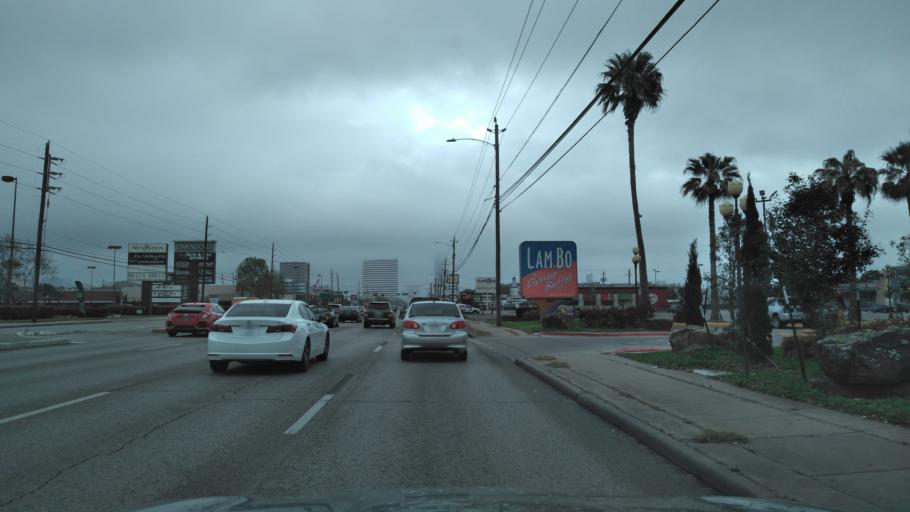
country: US
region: Texas
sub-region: Harris County
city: Hunters Creek Village
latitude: 29.7376
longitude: -95.4919
